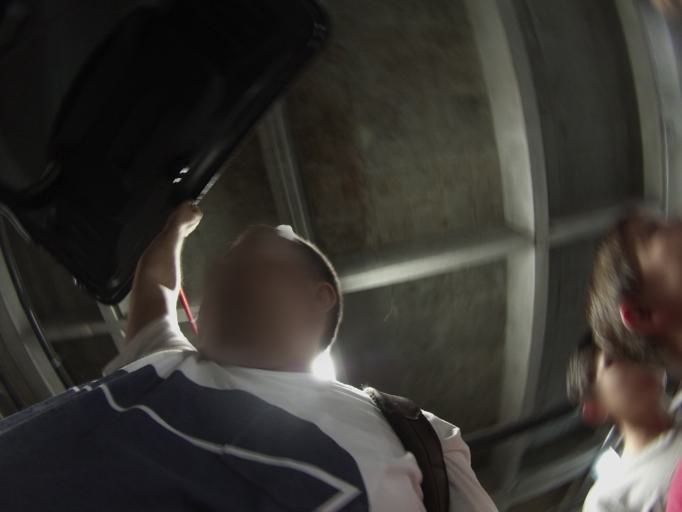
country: CO
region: Quindio
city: Armenia
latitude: 4.5422
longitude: -75.6666
